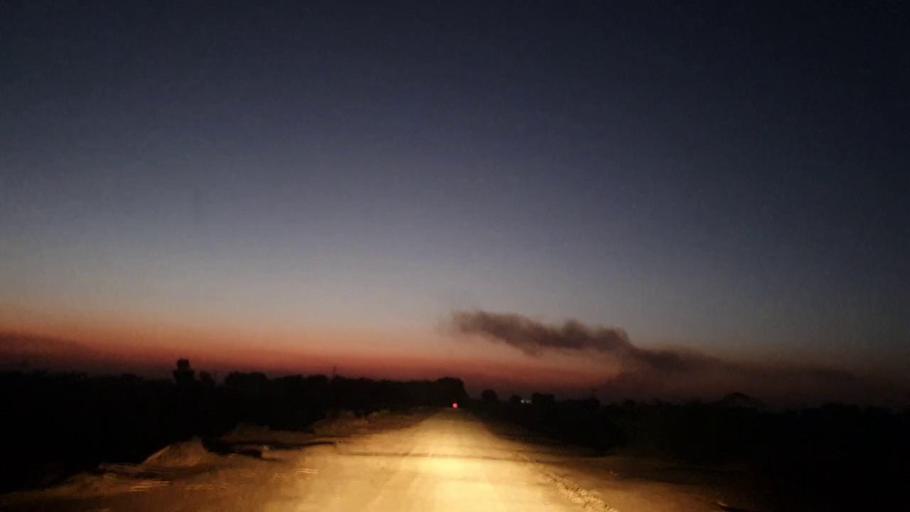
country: PK
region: Sindh
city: Nawabshah
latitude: 26.3184
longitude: 68.3671
